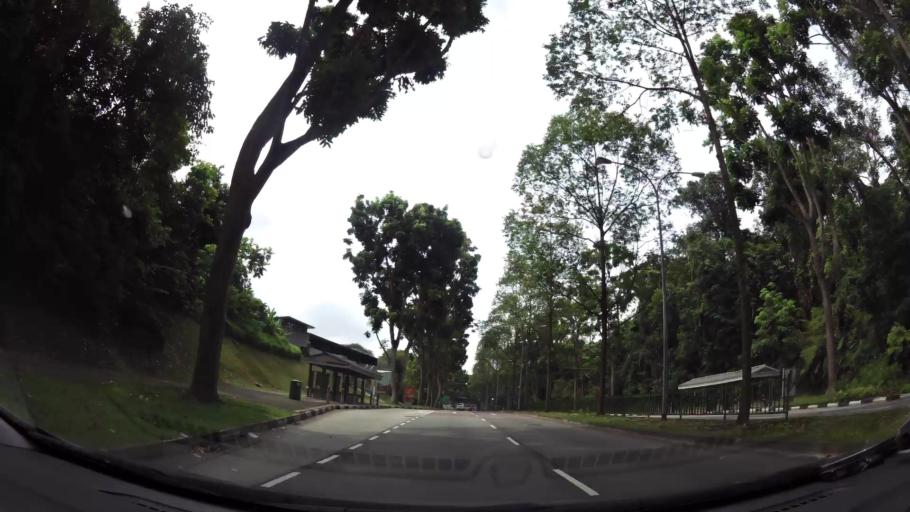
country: SG
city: Singapore
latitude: 1.3481
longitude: 103.7688
